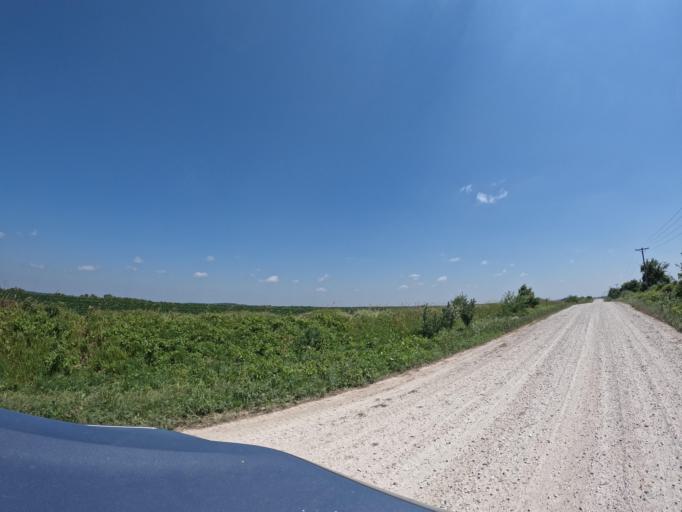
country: US
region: Iowa
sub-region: Keokuk County
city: Sigourney
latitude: 41.2794
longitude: -92.2325
